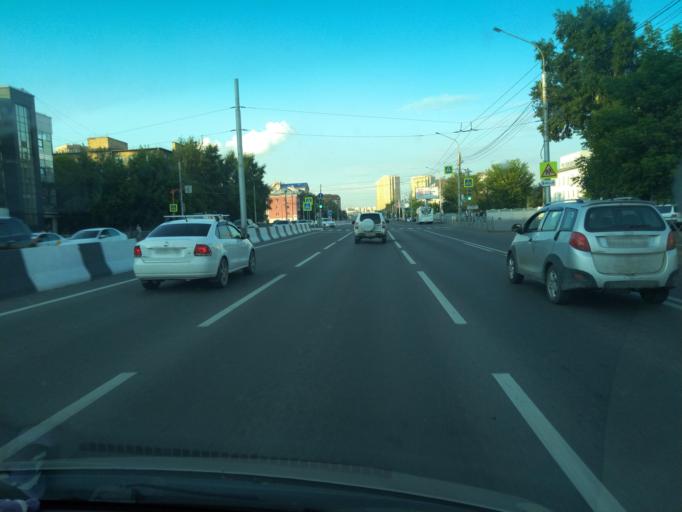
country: RU
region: Krasnoyarskiy
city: Krasnoyarsk
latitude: 56.0273
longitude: 92.9098
